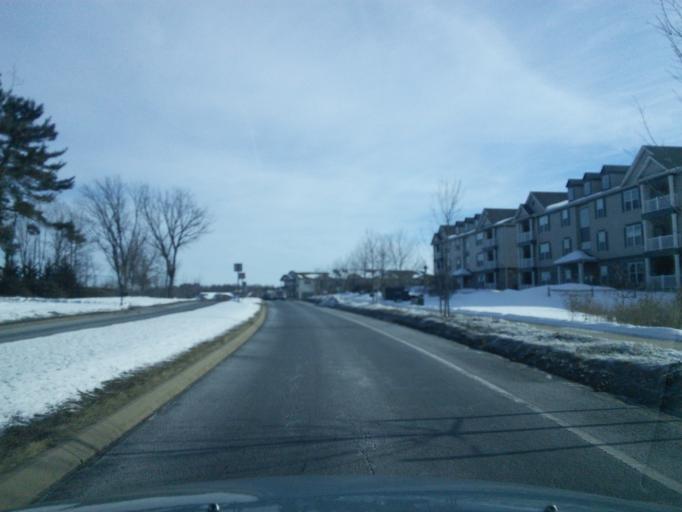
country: US
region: Pennsylvania
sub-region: Centre County
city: State College
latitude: 40.8250
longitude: -77.8816
